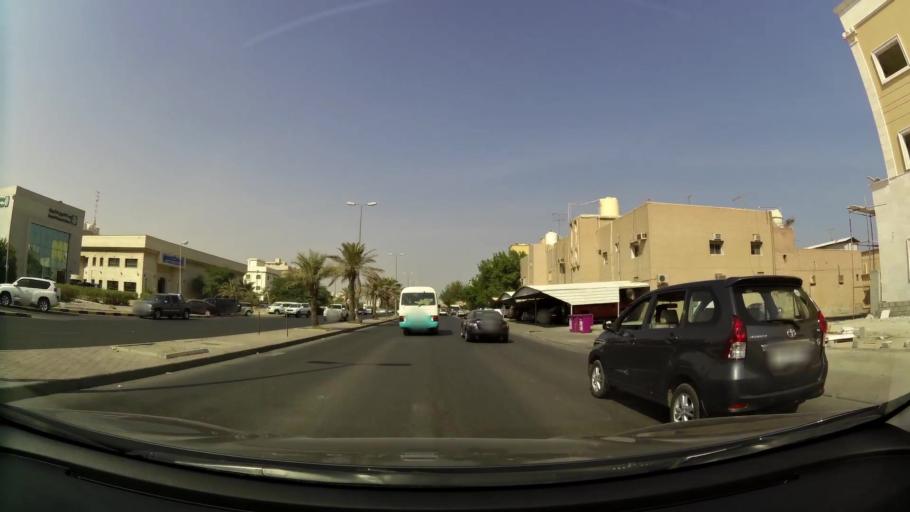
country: KW
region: Al Ahmadi
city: Al Fahahil
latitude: 29.0883
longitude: 48.1227
